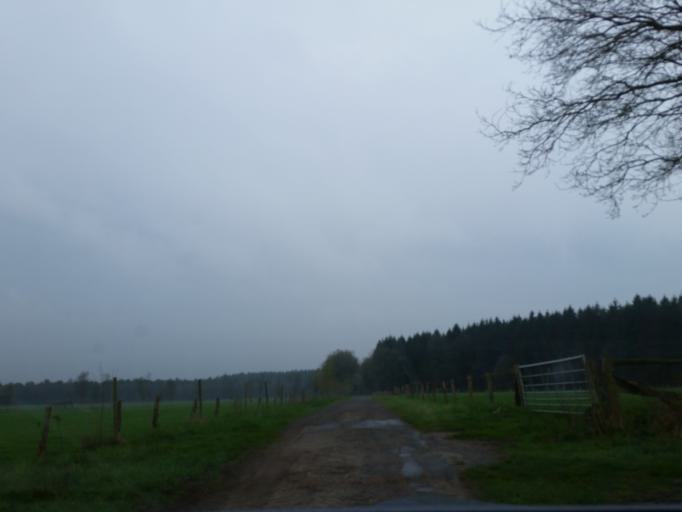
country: DE
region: Lower Saxony
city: Stinstedt
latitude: 53.5941
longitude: 8.9668
